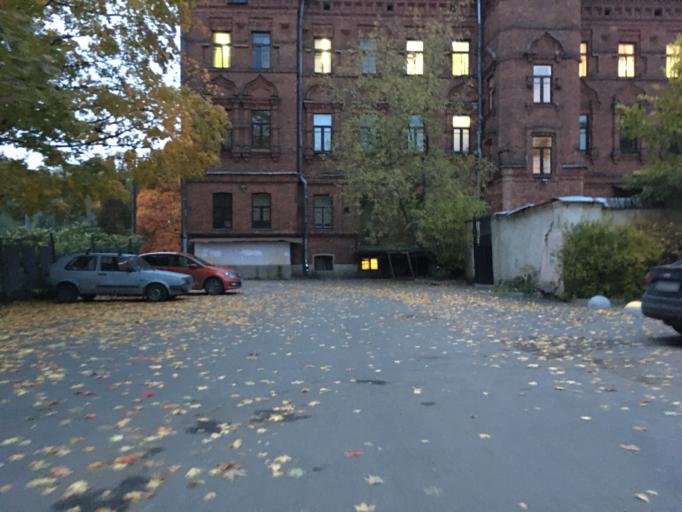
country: RU
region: St.-Petersburg
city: Centralniy
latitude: 59.9043
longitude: 30.3657
